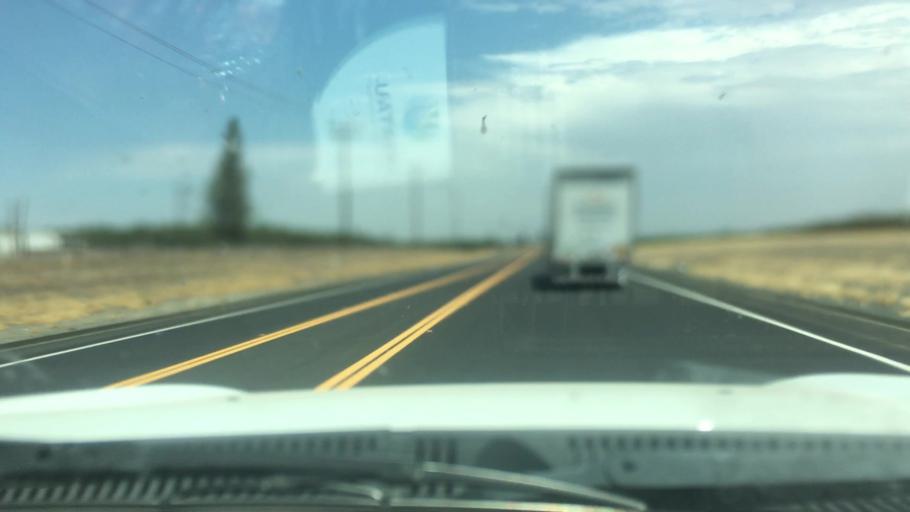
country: US
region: California
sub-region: Tulare County
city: Terra Bella
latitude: 35.9270
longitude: -119.0536
